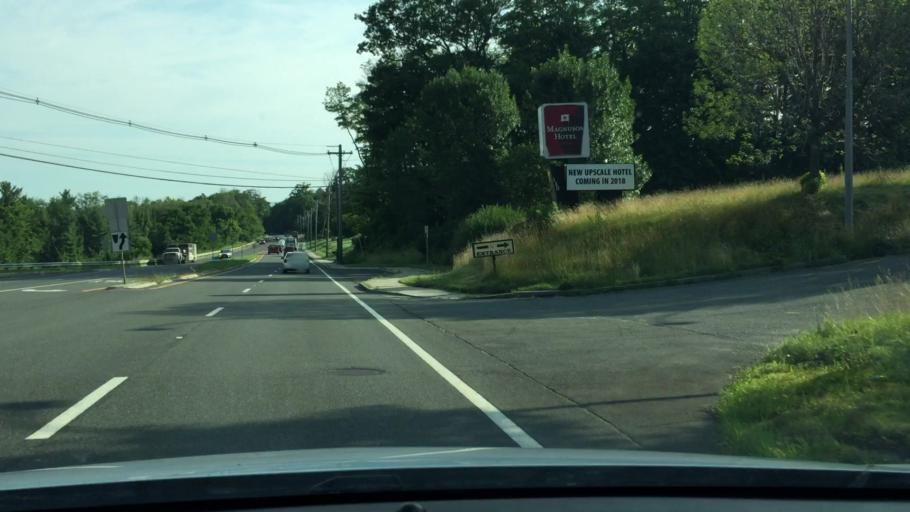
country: US
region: Massachusetts
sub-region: Berkshire County
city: Lenox
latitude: 42.3819
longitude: -73.2761
